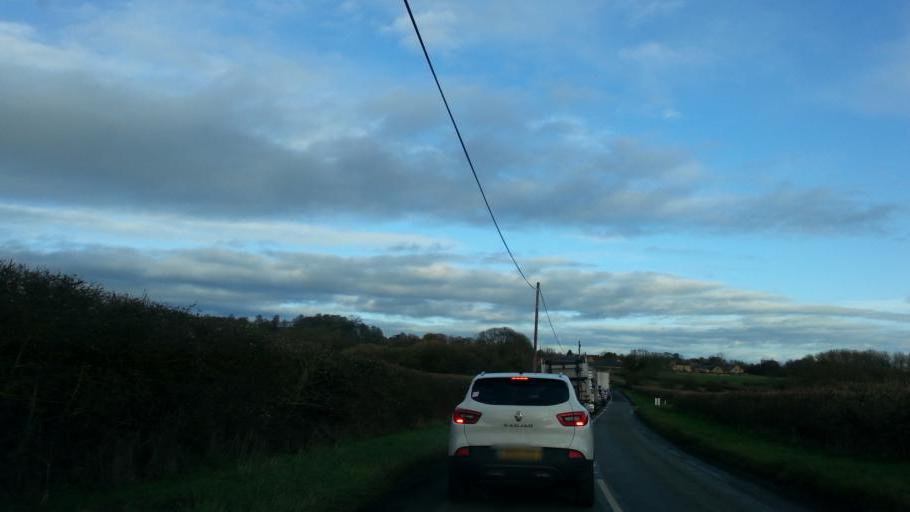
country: GB
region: England
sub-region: Oxfordshire
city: Faringdon
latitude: 51.6212
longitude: -1.5890
